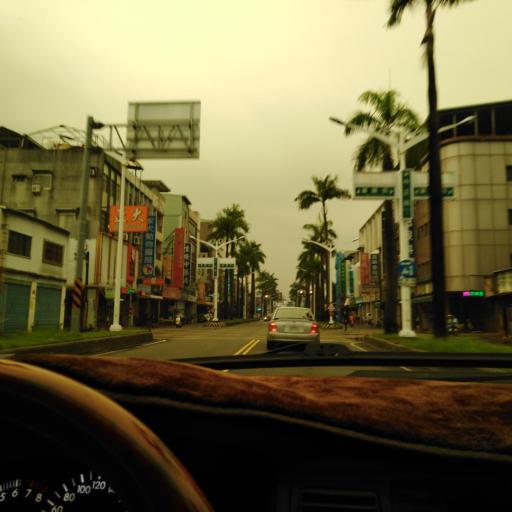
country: TW
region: Taiwan
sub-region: Pingtung
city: Pingtung
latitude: 22.6793
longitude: 120.4912
